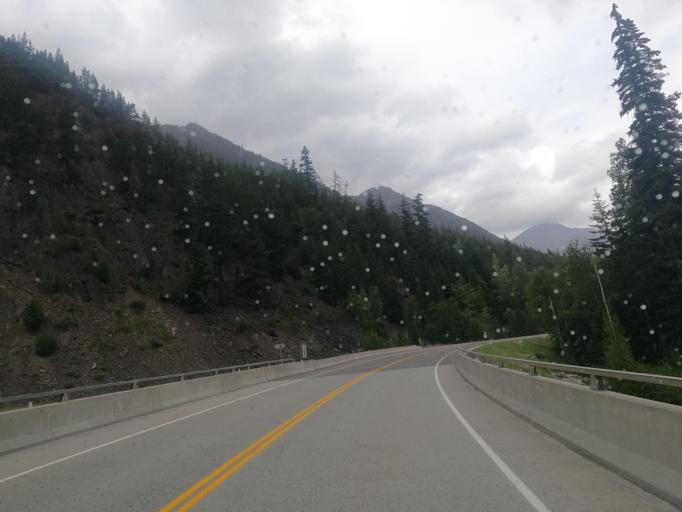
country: CA
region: British Columbia
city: Lillooet
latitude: 50.5002
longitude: -122.1851
